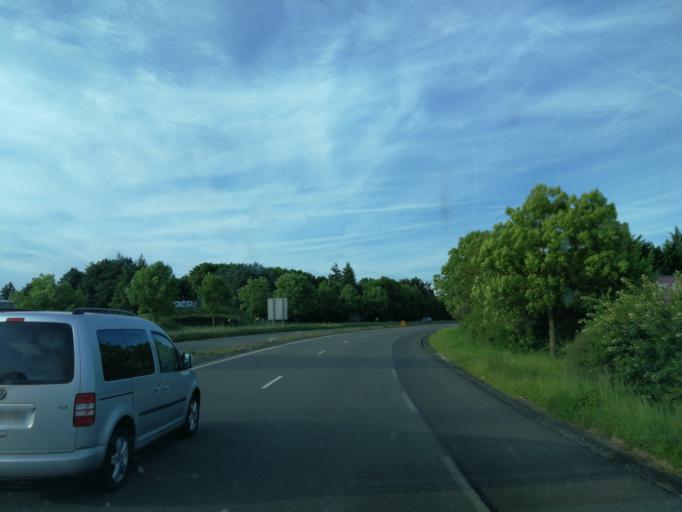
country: FR
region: Centre
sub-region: Departement d'Eure-et-Loir
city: Le Coudray
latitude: 48.4401
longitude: 1.5216
